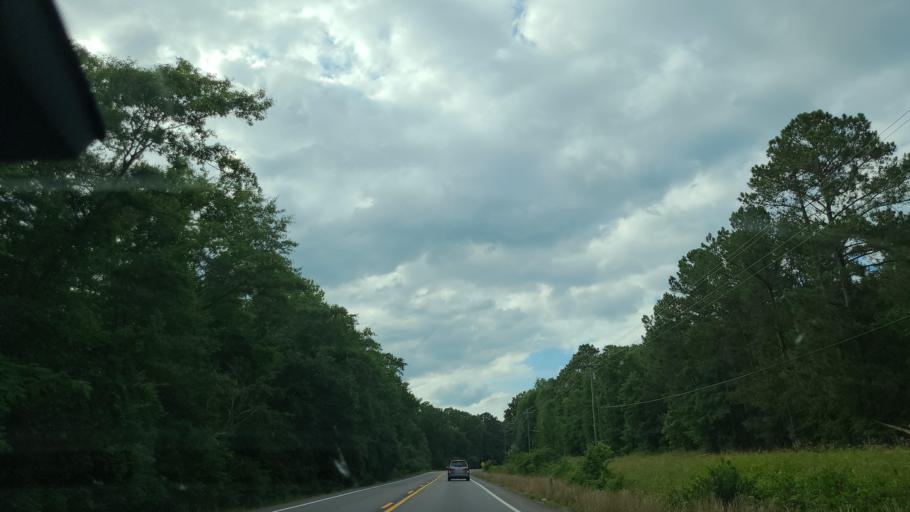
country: US
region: Georgia
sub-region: Putnam County
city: Eatonton
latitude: 33.2320
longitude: -83.4343
